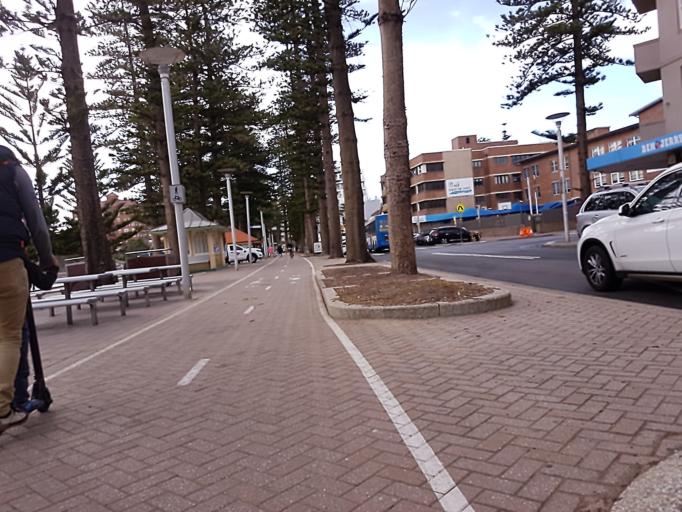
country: AU
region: New South Wales
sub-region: Manly Vale
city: Manly
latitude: -33.7978
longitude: 151.2885
